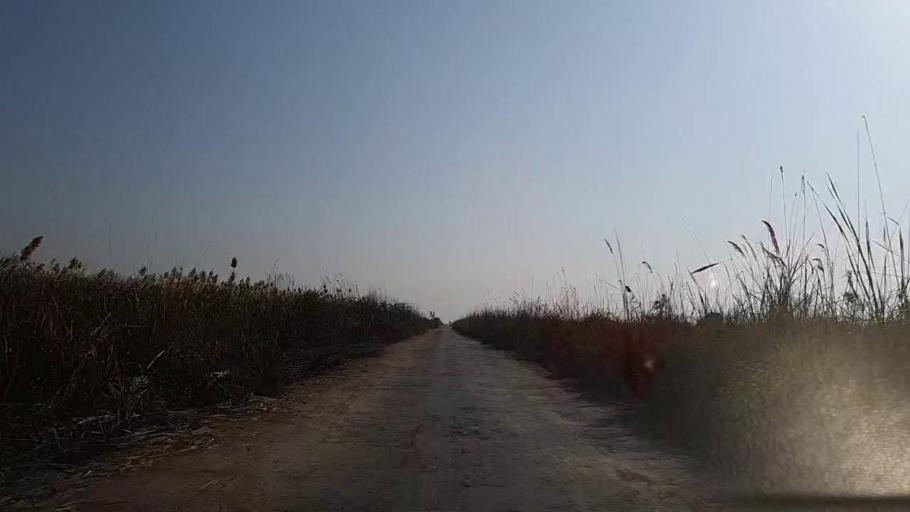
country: PK
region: Sindh
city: Tando Mittha Khan
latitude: 25.8942
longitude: 69.0770
